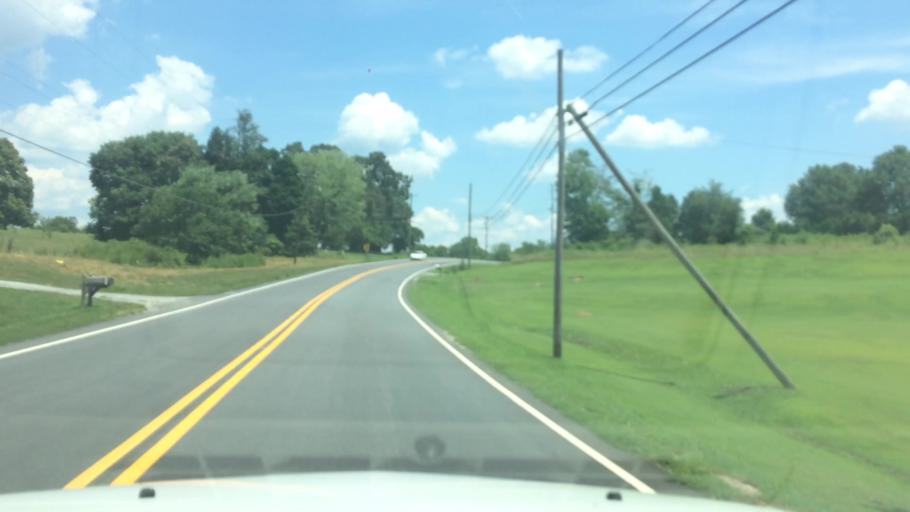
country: US
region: North Carolina
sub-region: Alexander County
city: Taylorsville
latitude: 35.9203
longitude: -81.2437
